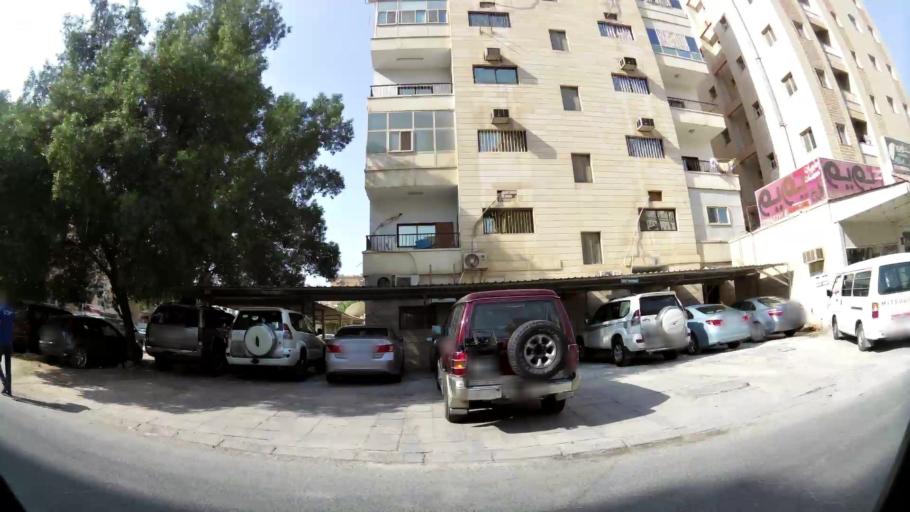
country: KW
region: Muhafazat Hawalli
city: Hawalli
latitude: 29.3324
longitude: 48.0235
